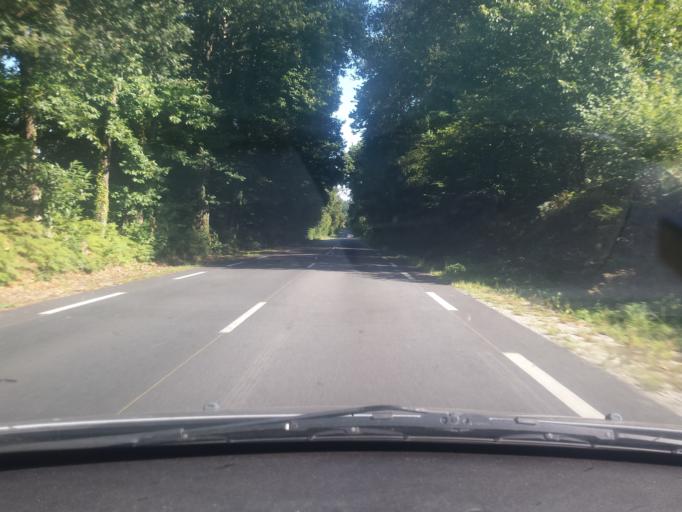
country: FR
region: Brittany
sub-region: Departement du Morbihan
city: Malguenac
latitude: 48.0986
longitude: -3.0560
